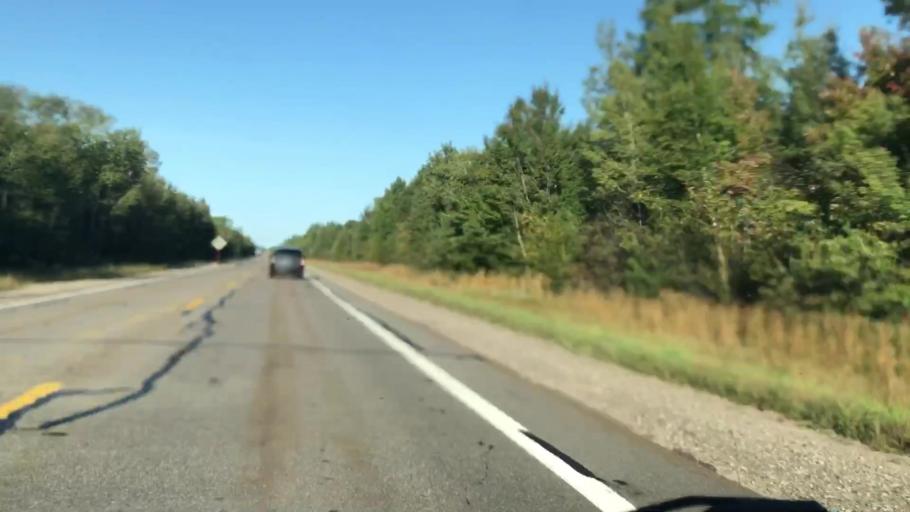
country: US
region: Michigan
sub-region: Chippewa County
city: Sault Ste. Marie
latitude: 46.3758
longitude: -84.6297
